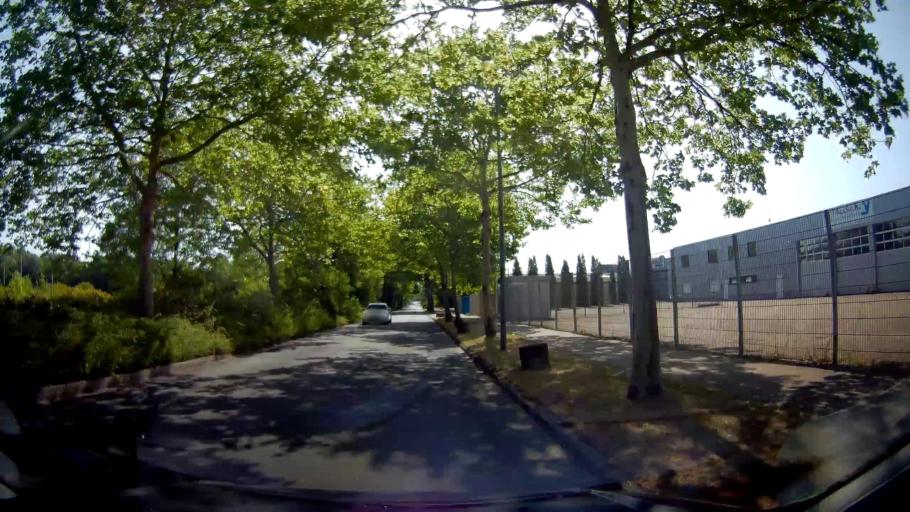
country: DE
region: North Rhine-Westphalia
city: Bochum-Hordel
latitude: 51.5115
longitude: 7.1920
